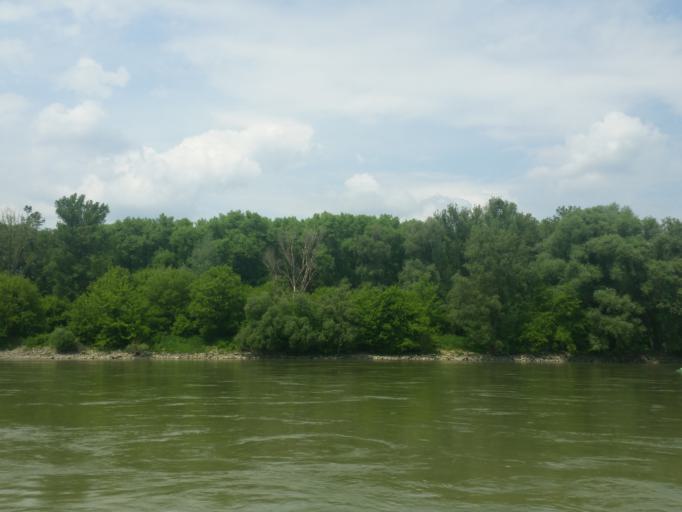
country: AT
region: Lower Austria
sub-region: Politischer Bezirk Bruck an der Leitha
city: Berg
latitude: 48.1424
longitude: 17.0521
